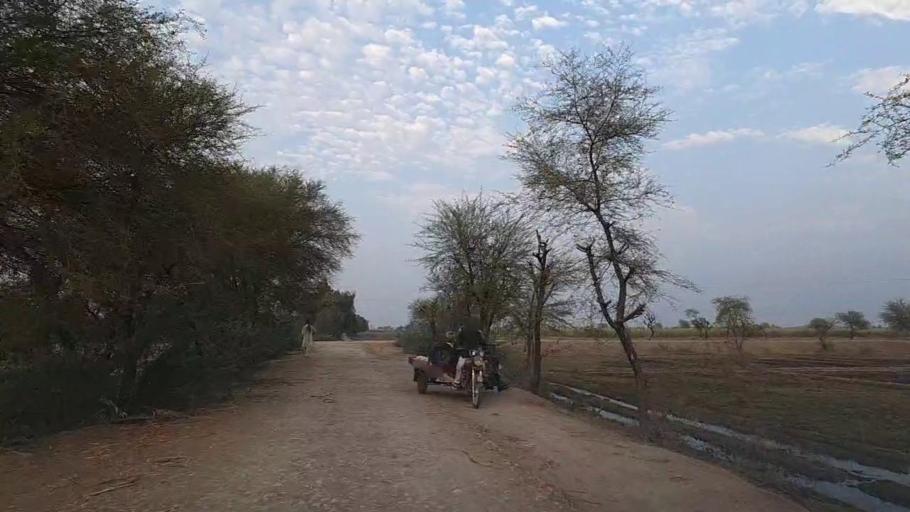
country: PK
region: Sindh
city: Mirwah Gorchani
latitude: 25.2981
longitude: 69.2222
